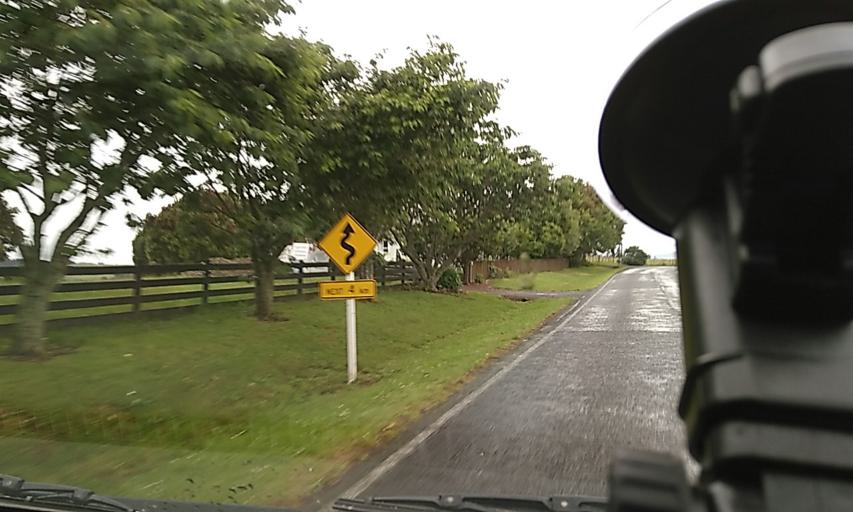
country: NZ
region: Auckland
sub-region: Auckland
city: Pukekohe East
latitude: -37.3237
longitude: 174.9181
